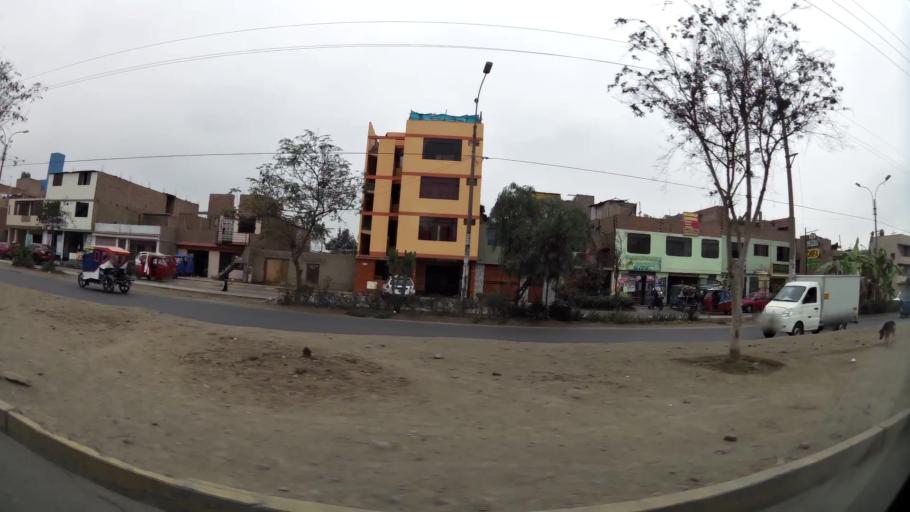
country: PE
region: Lima
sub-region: Lima
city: Independencia
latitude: -11.9456
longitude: -77.0624
